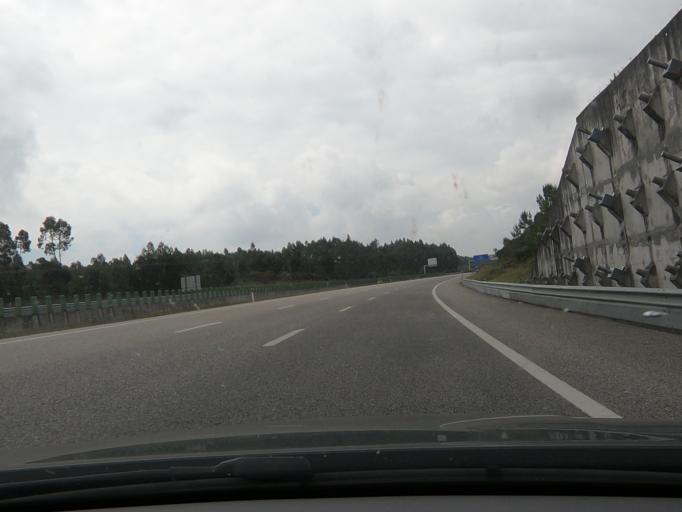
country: PT
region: Leiria
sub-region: Pombal
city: Lourical
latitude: 39.9516
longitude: -8.7718
